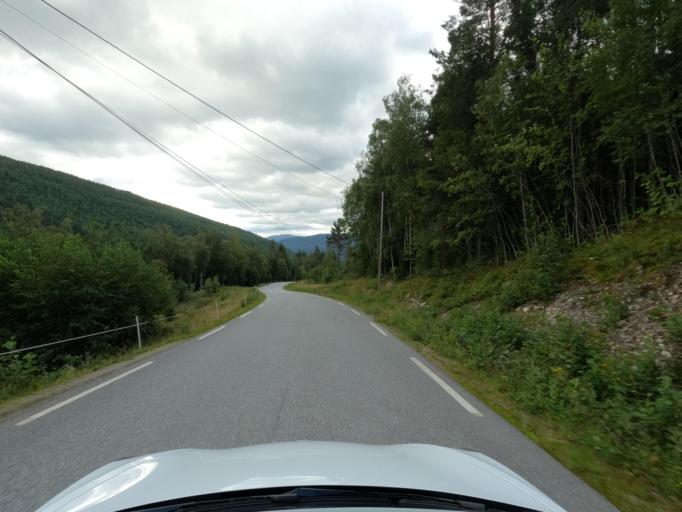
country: NO
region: Telemark
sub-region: Tinn
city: Rjukan
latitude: 60.0251
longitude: 8.7390
